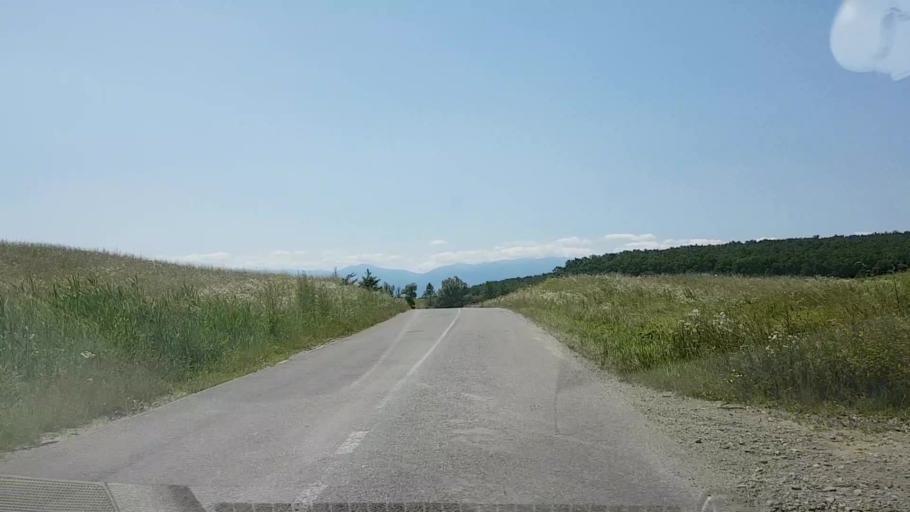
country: RO
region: Brasov
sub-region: Comuna Cincu
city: Cincu
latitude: 45.8899
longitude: 24.8119
